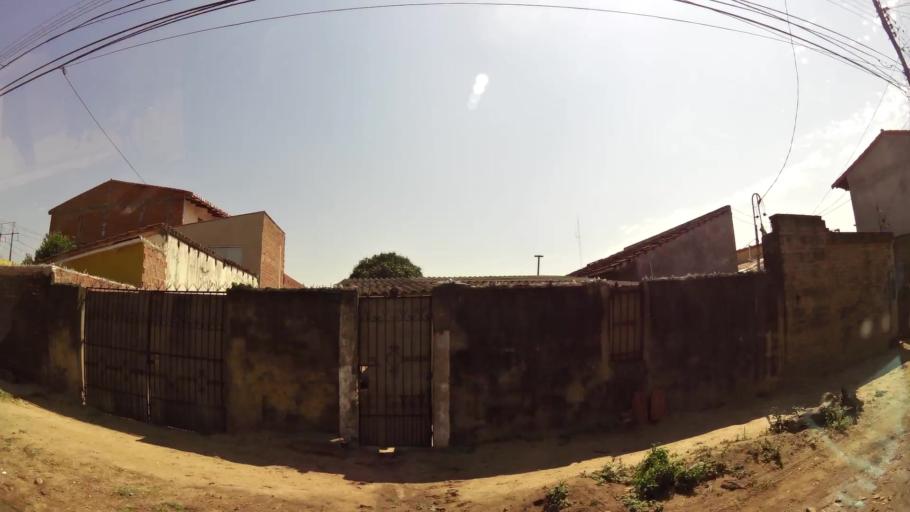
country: BO
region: Santa Cruz
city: Santa Cruz de la Sierra
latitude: -17.7460
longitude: -63.1551
